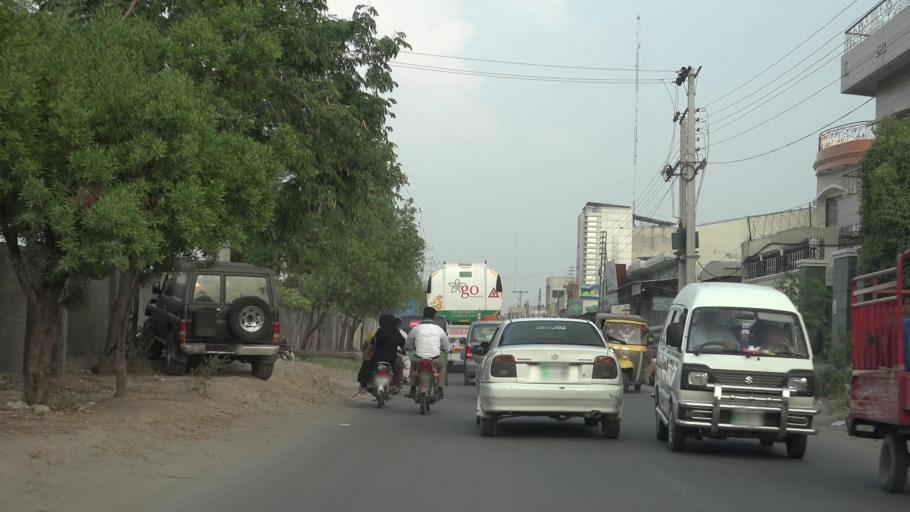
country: PK
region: Punjab
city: Faisalabad
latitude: 31.4444
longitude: 73.1303
